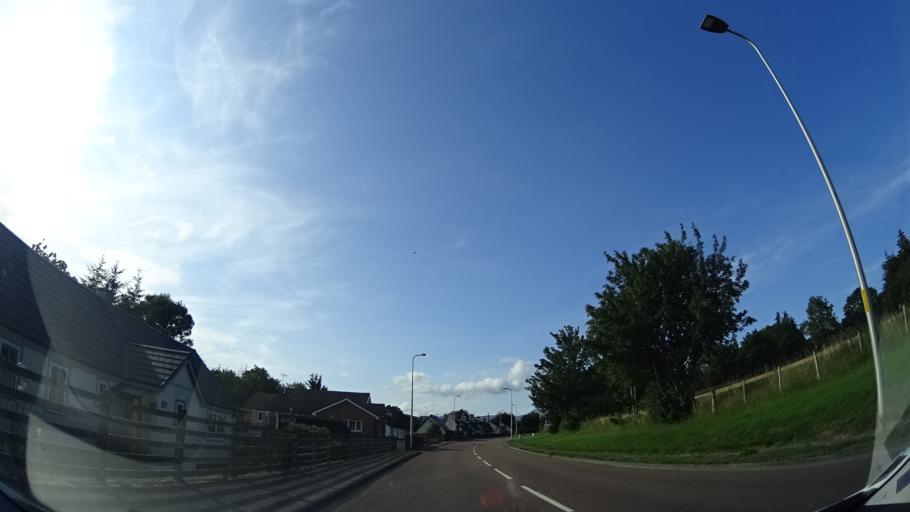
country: GB
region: Scotland
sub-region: Highland
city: Muir of Ord
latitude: 57.5648
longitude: -4.5776
